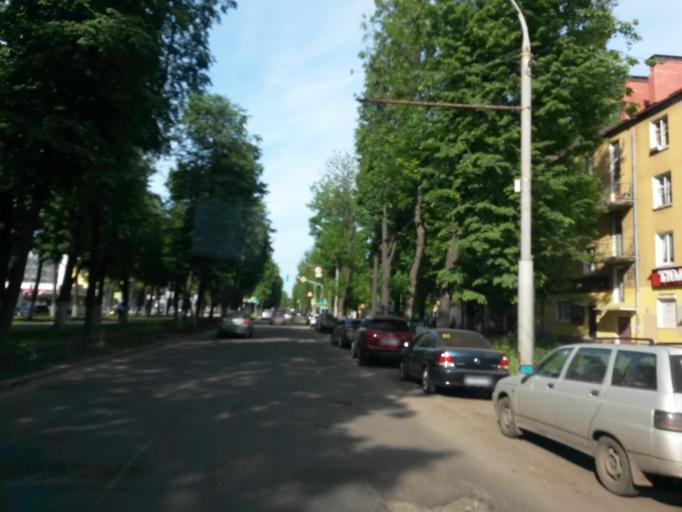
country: RU
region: Jaroslavl
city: Yaroslavl
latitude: 57.6378
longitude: 39.8699
